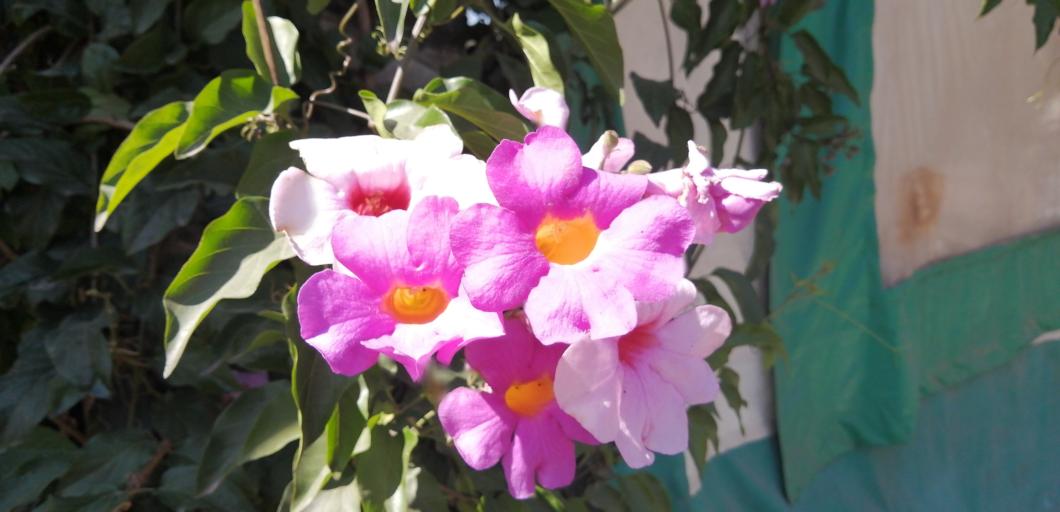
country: MX
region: Mexico
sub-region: Teotihuacan
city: Teotihuacan de Arista
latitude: 19.6890
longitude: -98.8569
